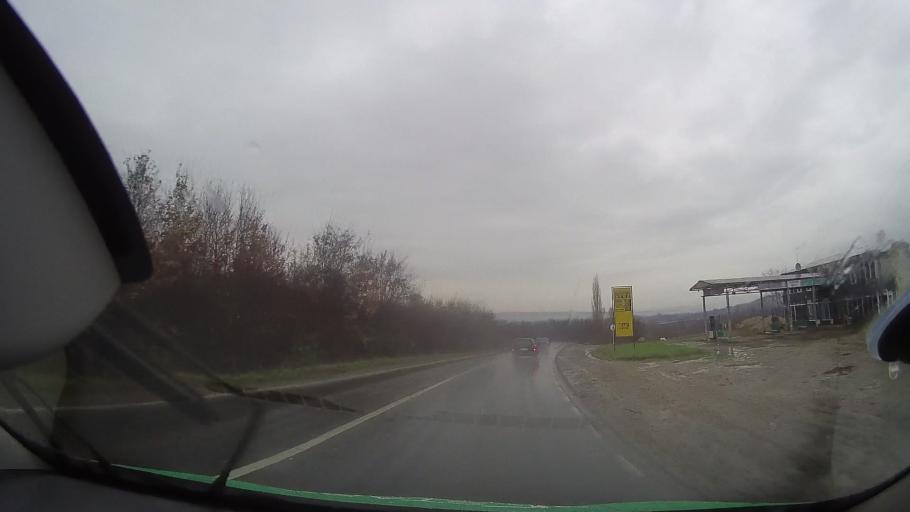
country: RO
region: Bihor
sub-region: Comuna Holod
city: Vintere
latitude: 46.7633
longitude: 22.1871
